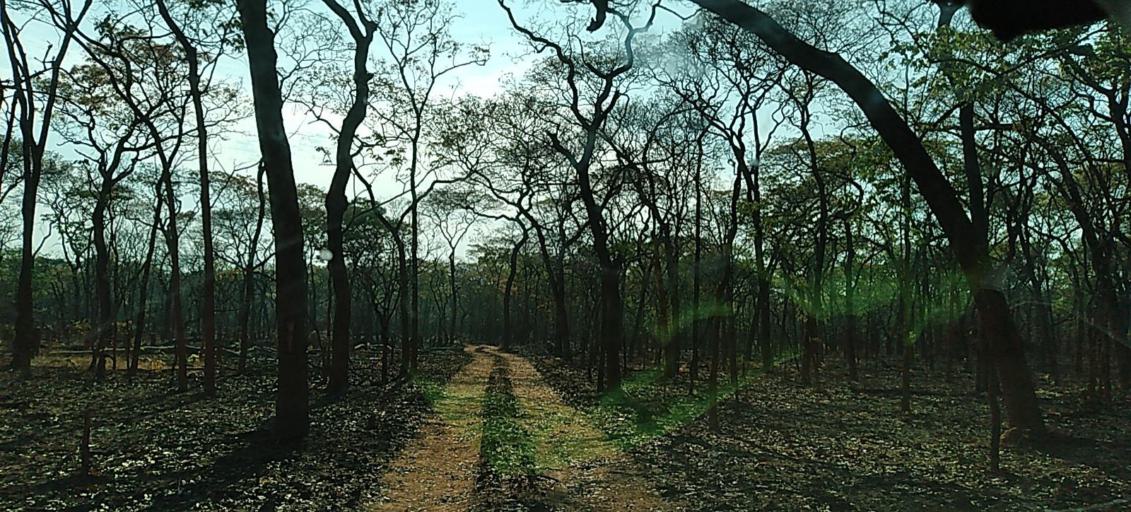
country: ZM
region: North-Western
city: Kalengwa
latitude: -13.2279
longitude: 25.0880
